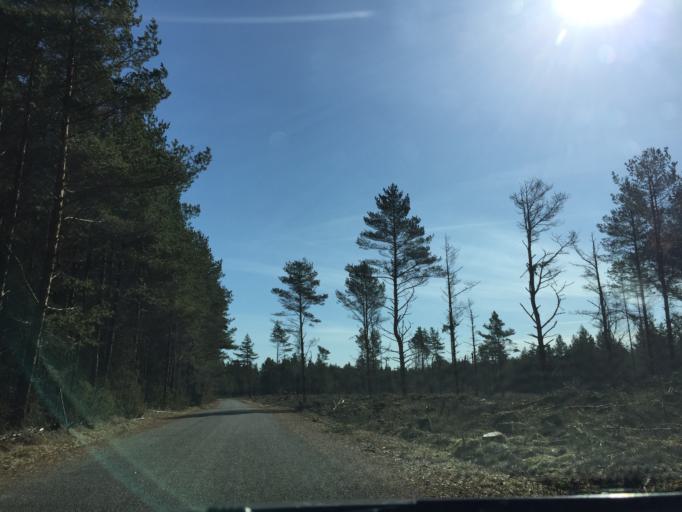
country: EE
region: Laeaene
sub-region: Lihula vald
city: Lihula
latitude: 58.6136
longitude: 23.5635
